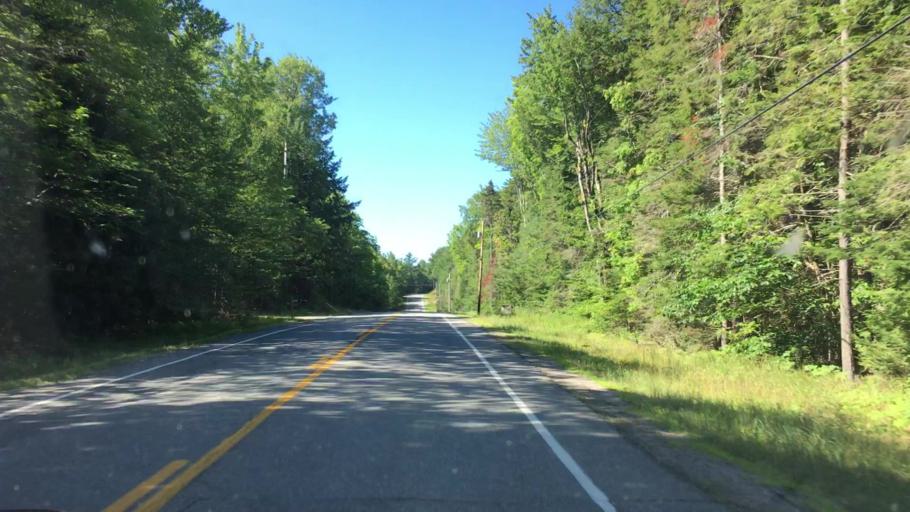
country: US
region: Maine
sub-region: Hancock County
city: Dedham
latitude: 44.6806
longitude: -68.6676
